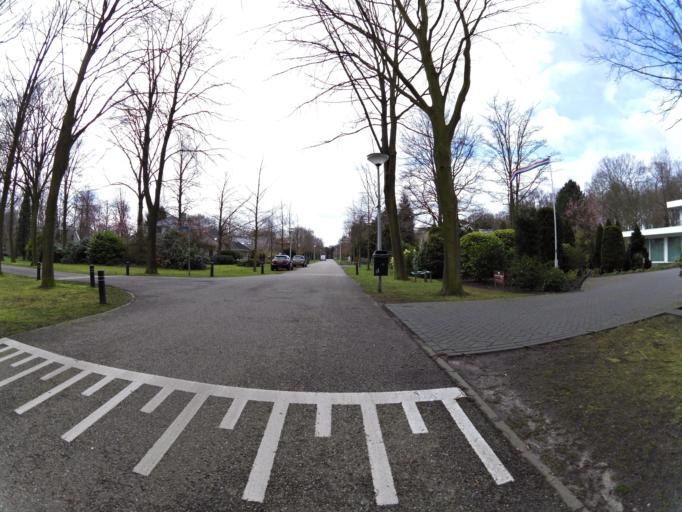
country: NL
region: South Holland
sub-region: Gemeente Brielle
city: Brielle
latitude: 51.9060
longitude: 4.0873
